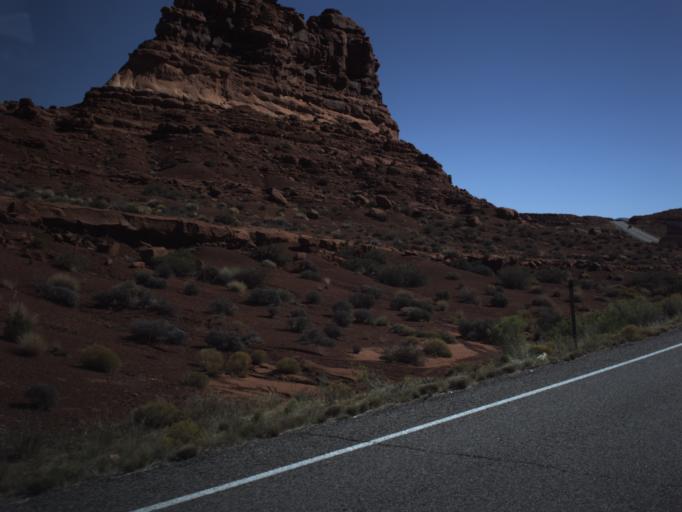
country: US
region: Utah
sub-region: San Juan County
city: Blanding
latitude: 37.8115
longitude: -110.3407
